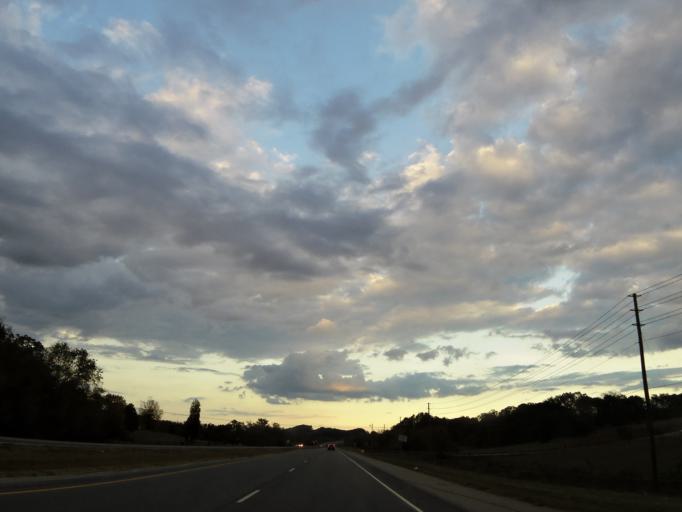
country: US
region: Tennessee
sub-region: Blount County
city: Louisville
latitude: 35.7516
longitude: -84.1071
